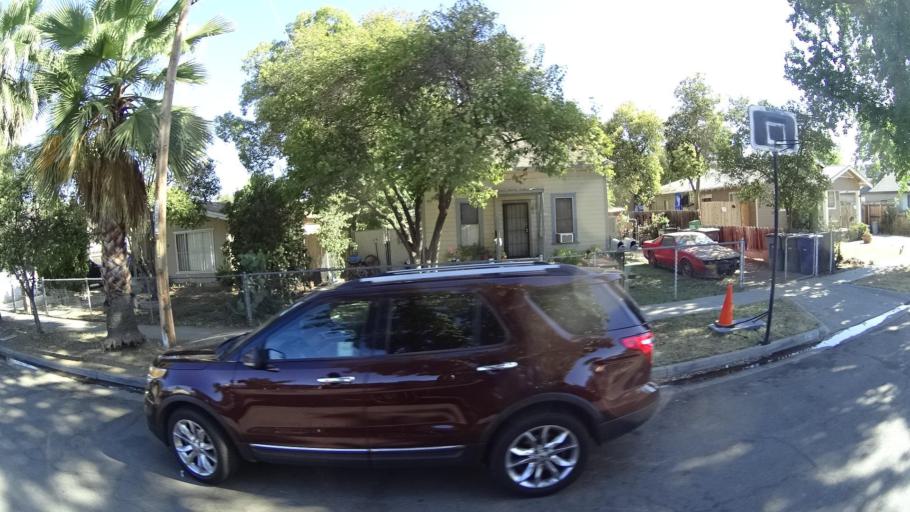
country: US
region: California
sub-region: Fresno County
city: Fresno
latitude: 36.7750
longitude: -119.7968
